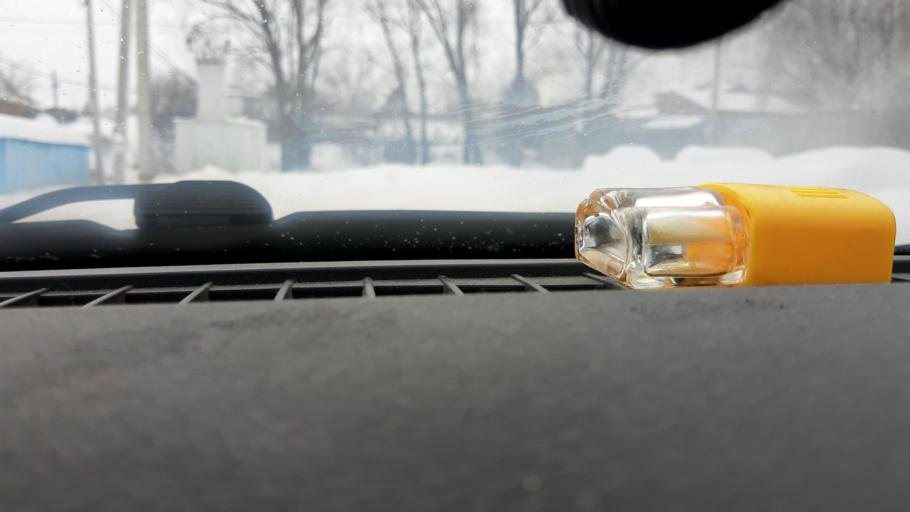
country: RU
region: Bashkortostan
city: Avdon
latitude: 54.7572
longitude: 55.7453
